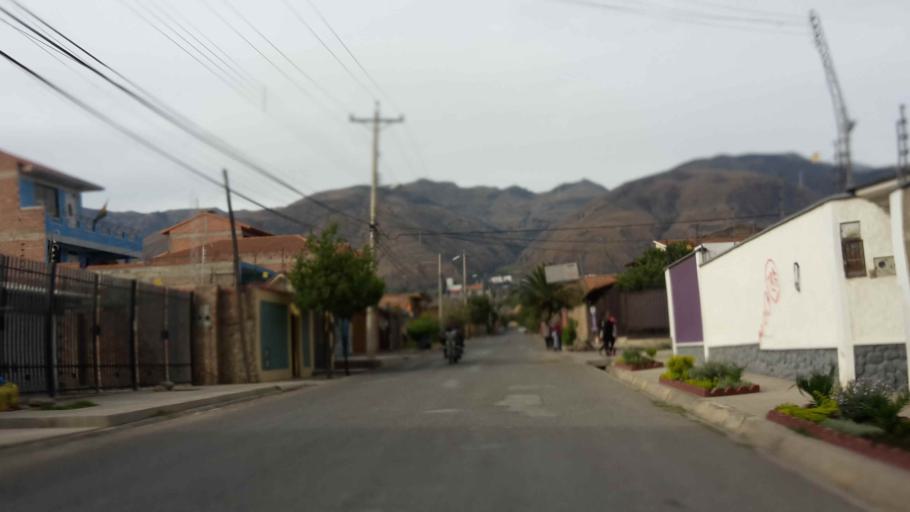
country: BO
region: Cochabamba
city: Cochabamba
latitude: -17.3565
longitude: -66.1952
